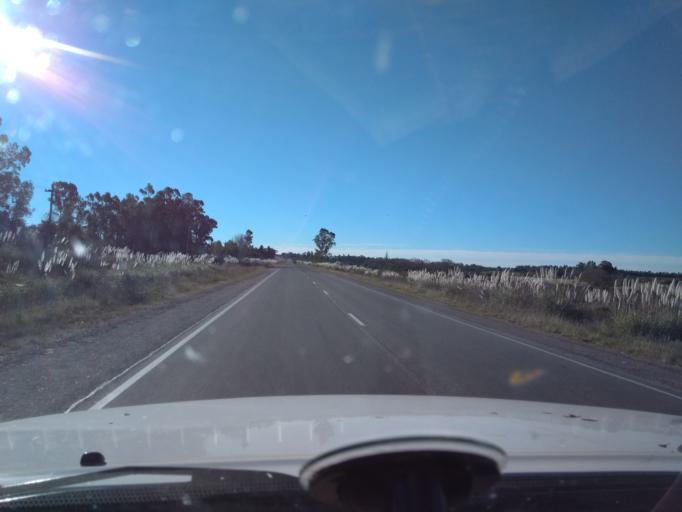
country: UY
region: Canelones
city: Sauce
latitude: -34.6044
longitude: -56.0491
